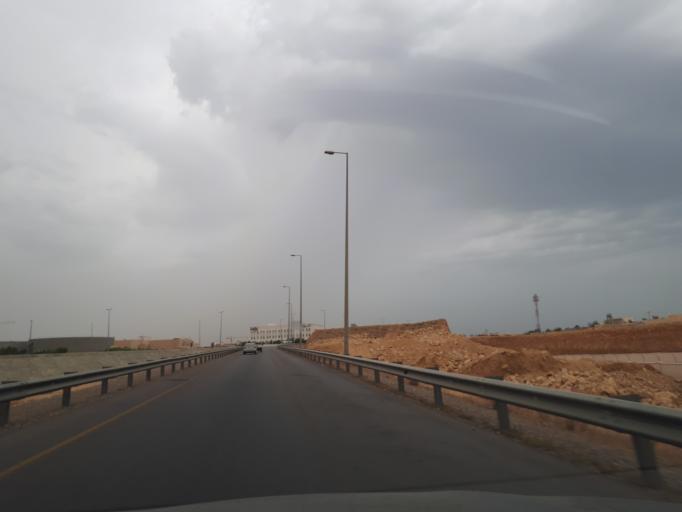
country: OM
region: Muhafazat Masqat
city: Bawshar
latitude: 23.5630
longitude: 58.3405
